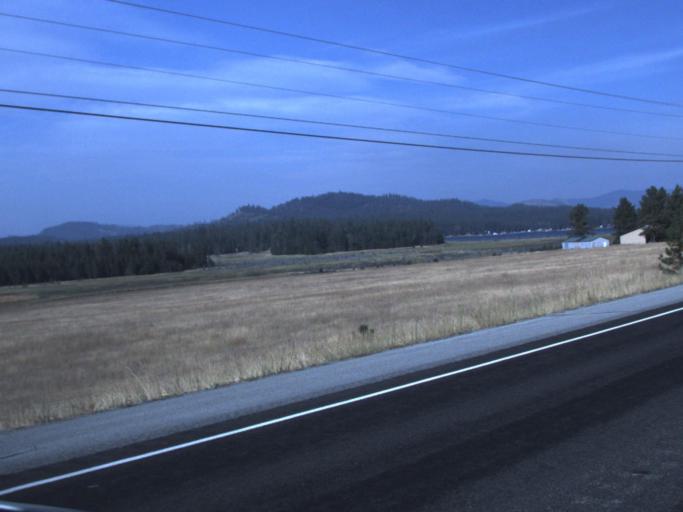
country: US
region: Washington
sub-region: Pend Oreille County
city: Newport
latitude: 48.1086
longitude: -117.2328
